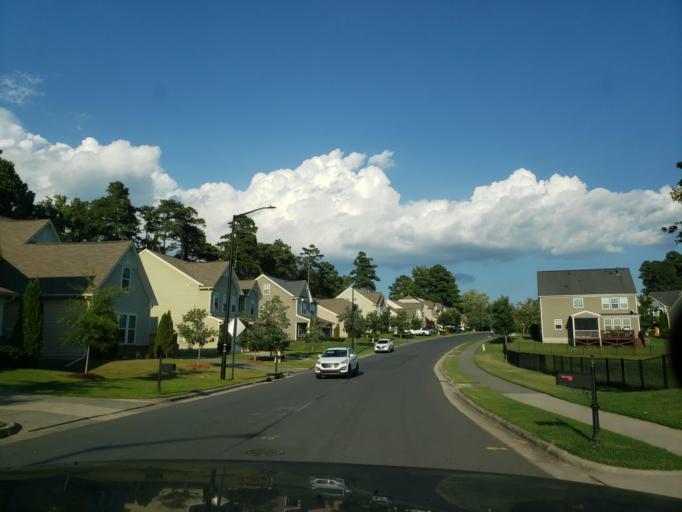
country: US
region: North Carolina
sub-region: Durham County
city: Durham
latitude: 35.9353
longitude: -78.9257
